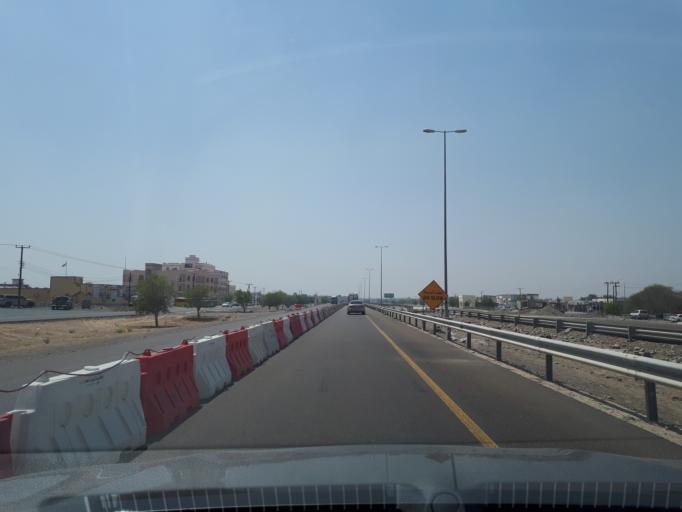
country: OM
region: Al Batinah
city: Al Liwa'
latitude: 24.5749
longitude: 56.5445
